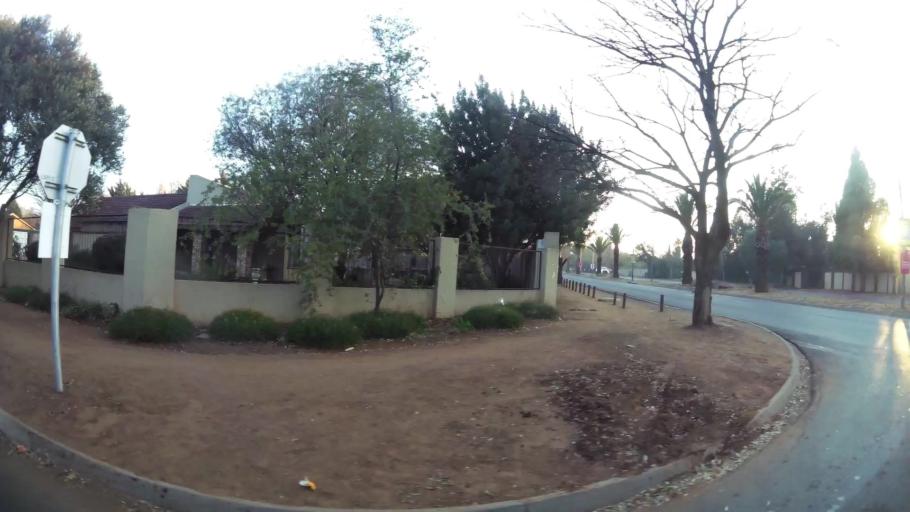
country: ZA
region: Orange Free State
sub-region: Mangaung Metropolitan Municipality
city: Bloemfontein
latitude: -29.1032
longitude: 26.1562
